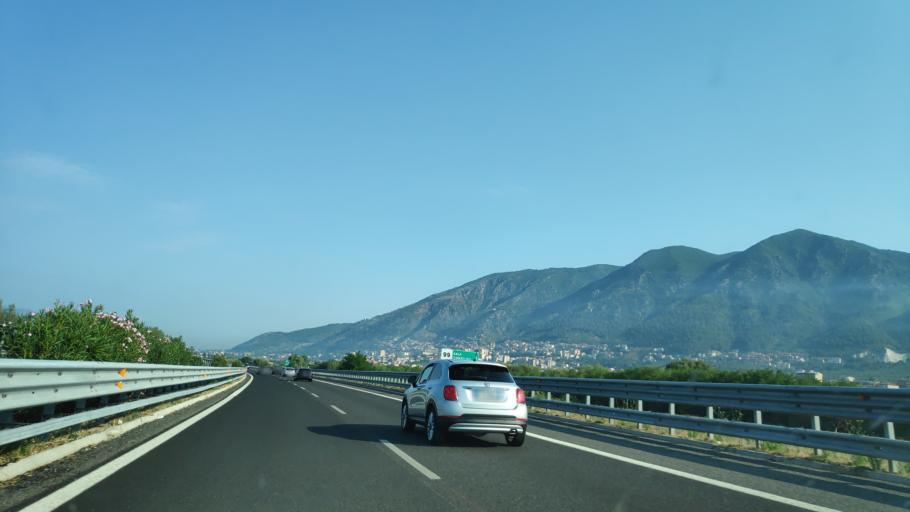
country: IT
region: Campania
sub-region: Provincia di Salerno
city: Sala Consilina
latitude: 40.3736
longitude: 15.5995
